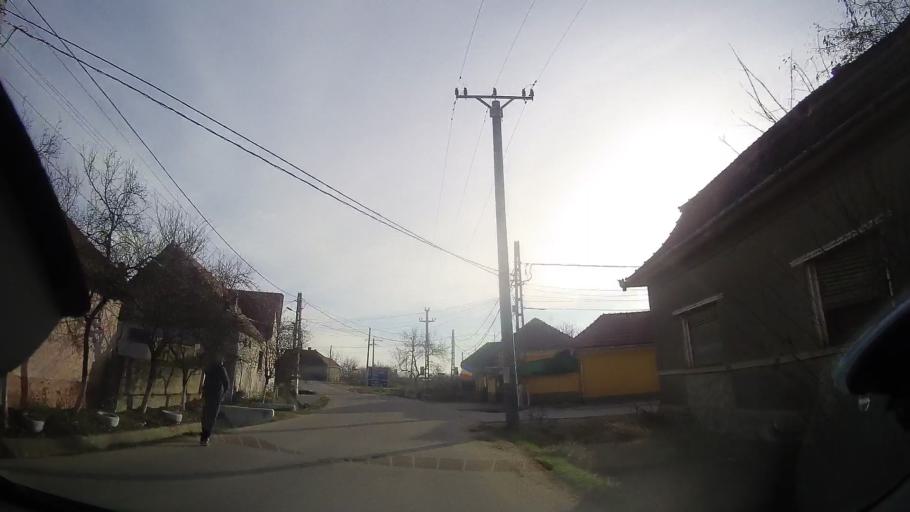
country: RO
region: Bihor
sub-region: Comuna Tileagd
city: Tileagd
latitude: 47.0817
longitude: 22.2027
